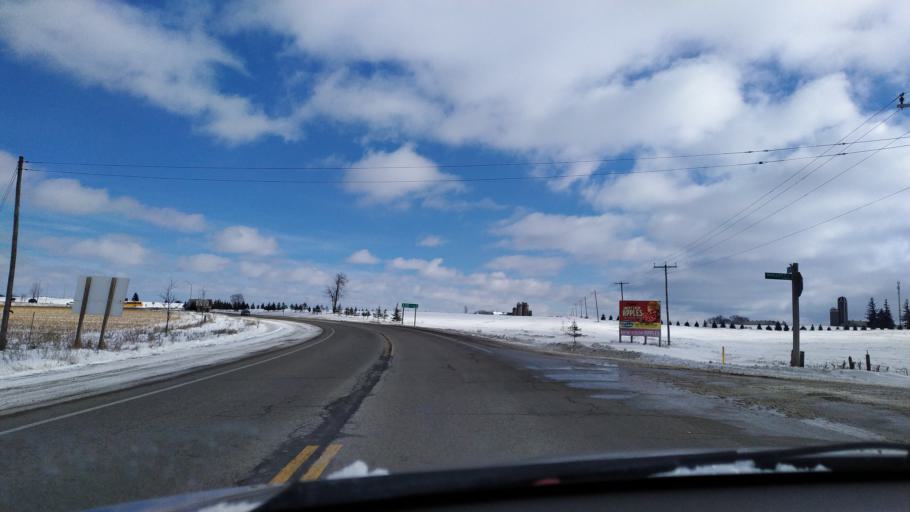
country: CA
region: Ontario
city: Waterloo
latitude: 43.5919
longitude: -80.6151
